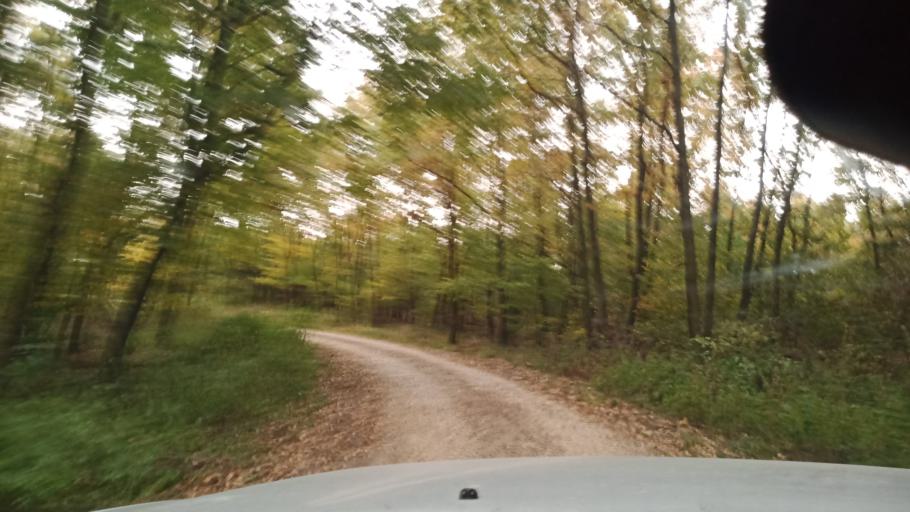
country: HU
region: Fejer
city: Mor
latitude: 47.3855
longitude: 18.2471
